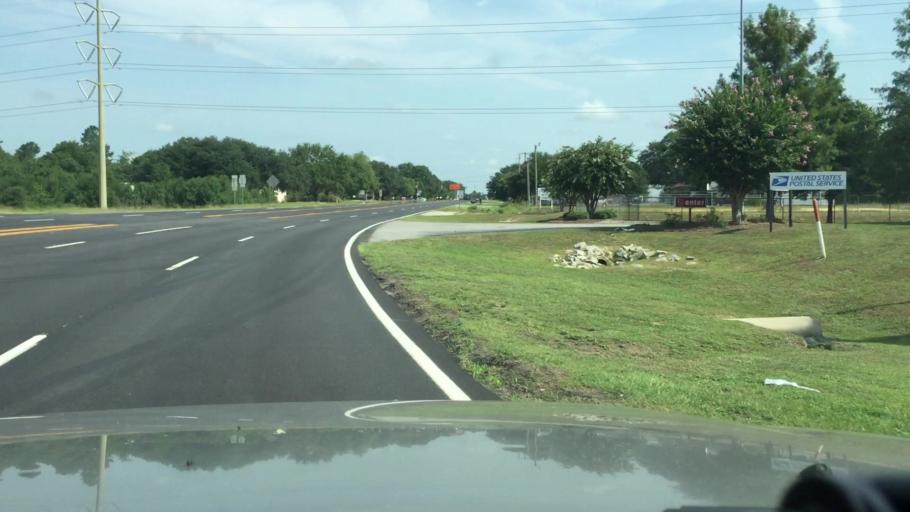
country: US
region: South Carolina
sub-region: Sumter County
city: South Sumter
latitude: 33.8851
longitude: -80.3498
